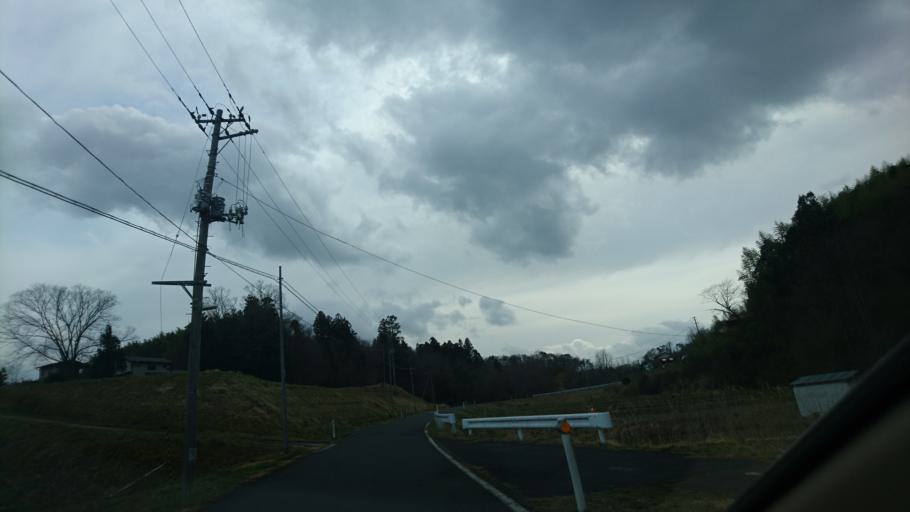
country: JP
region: Iwate
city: Ichinoseki
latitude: 38.8848
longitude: 141.1673
